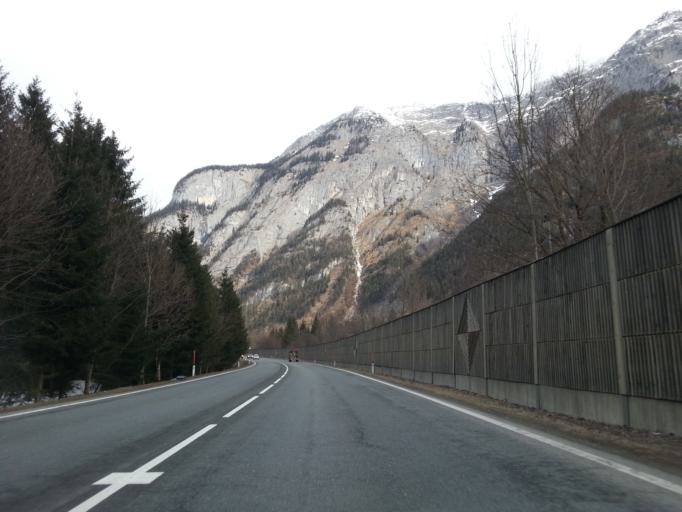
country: AT
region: Salzburg
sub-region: Politischer Bezirk Zell am See
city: Saalfelden am Steinernen Meer
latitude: 47.4790
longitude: 12.8317
